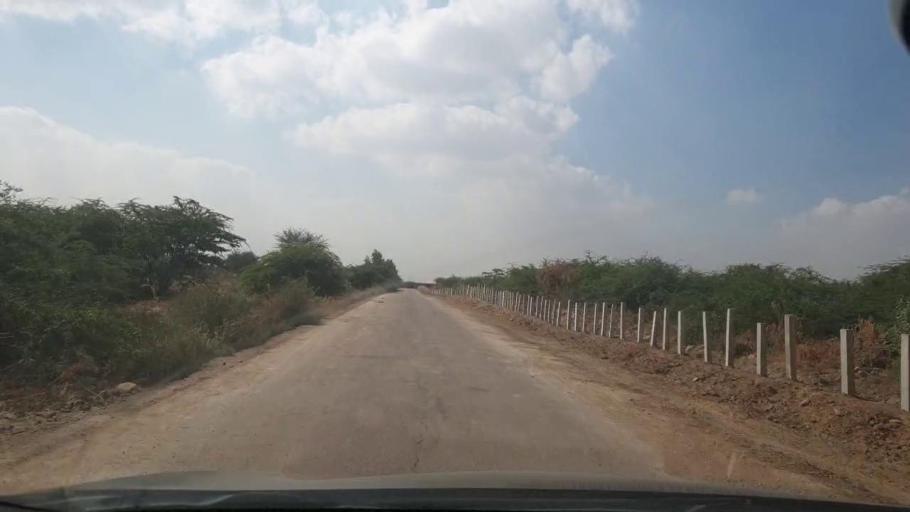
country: PK
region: Sindh
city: Malir Cantonment
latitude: 25.0239
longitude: 67.3577
